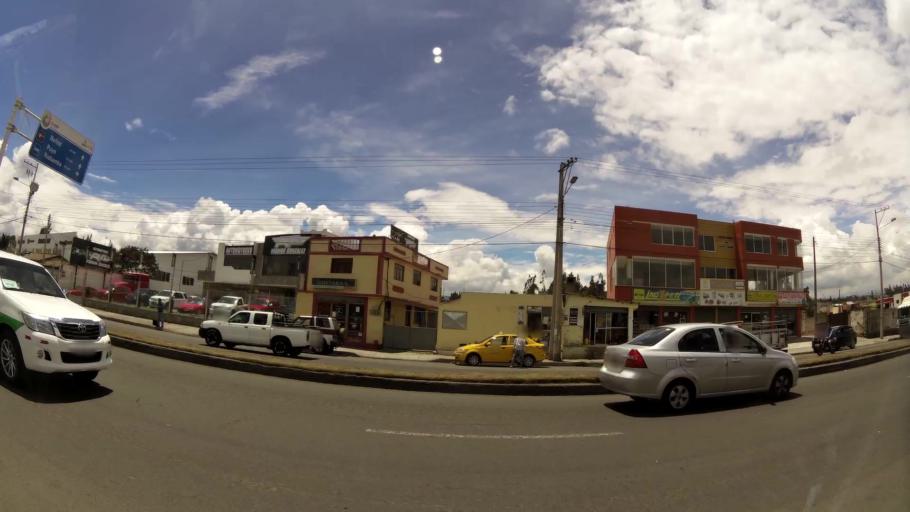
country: EC
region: Tungurahua
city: Ambato
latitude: -1.2872
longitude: -78.6052
